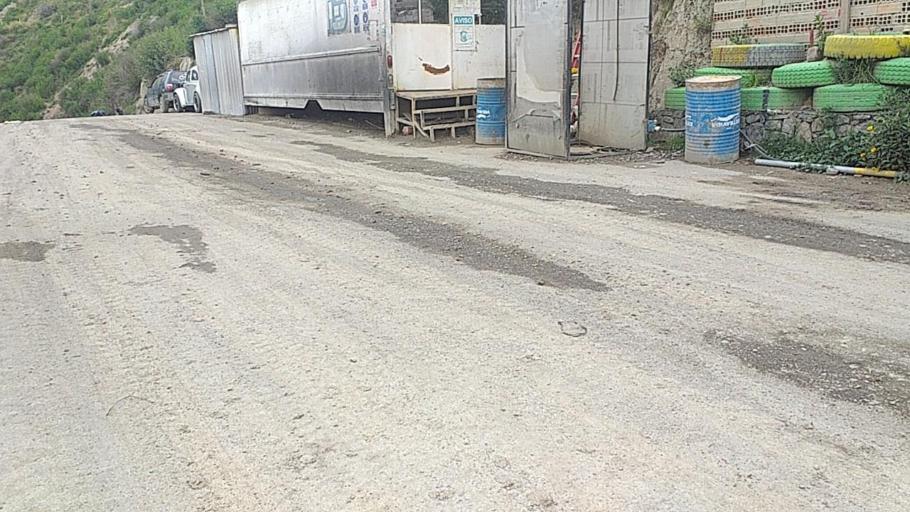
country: BO
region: La Paz
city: La Paz
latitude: -16.5384
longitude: -68.1390
